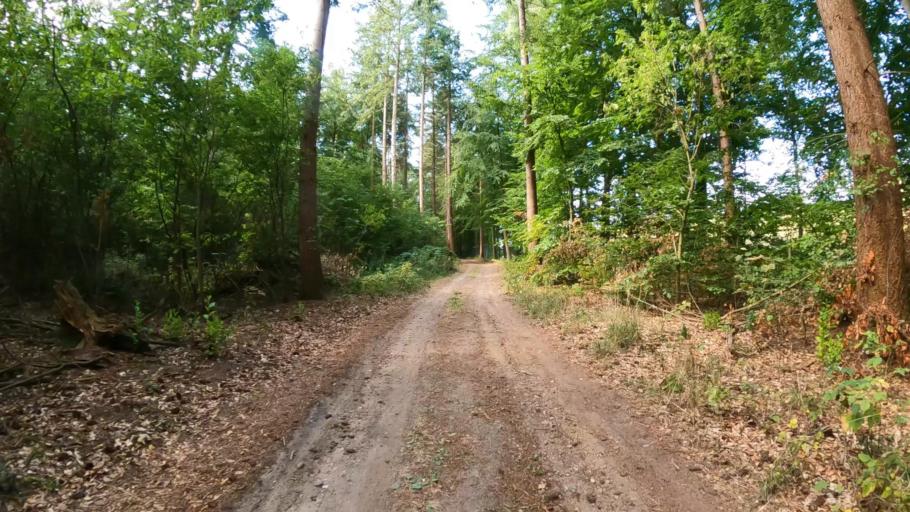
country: DE
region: Lower Saxony
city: Tespe
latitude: 53.4232
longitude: 10.4057
